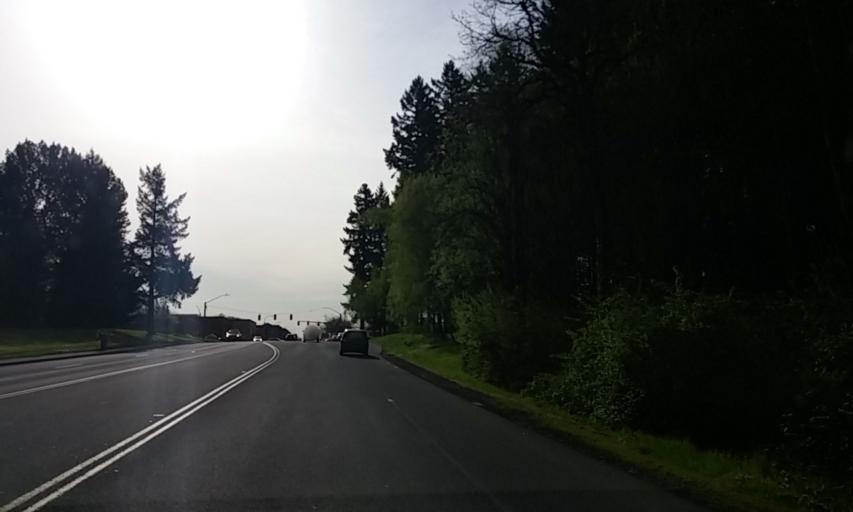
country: US
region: Oregon
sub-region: Washington County
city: Cedar Mill
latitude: 45.5044
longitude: -122.8289
